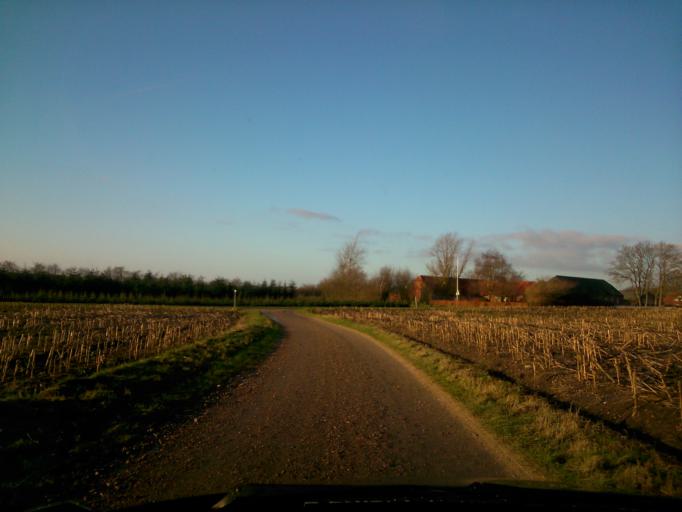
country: DK
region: Central Jutland
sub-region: Ringkobing-Skjern Kommune
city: Skjern
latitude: 55.9832
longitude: 8.5360
